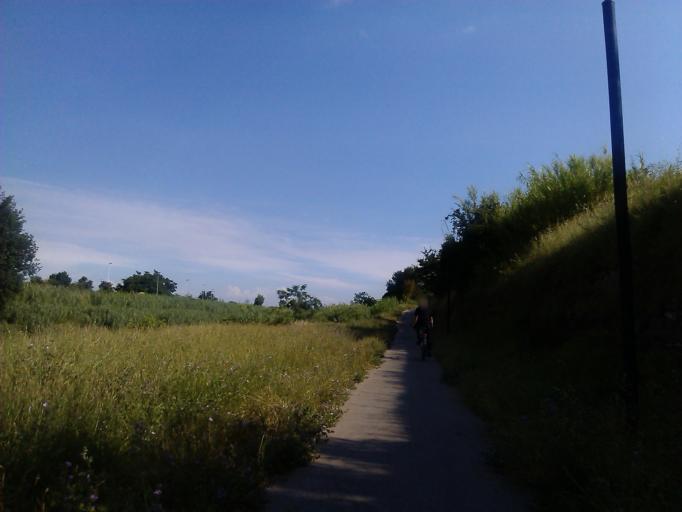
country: IT
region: Tuscany
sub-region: Provincia di Prato
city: Prato
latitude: 43.8685
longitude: 11.1171
